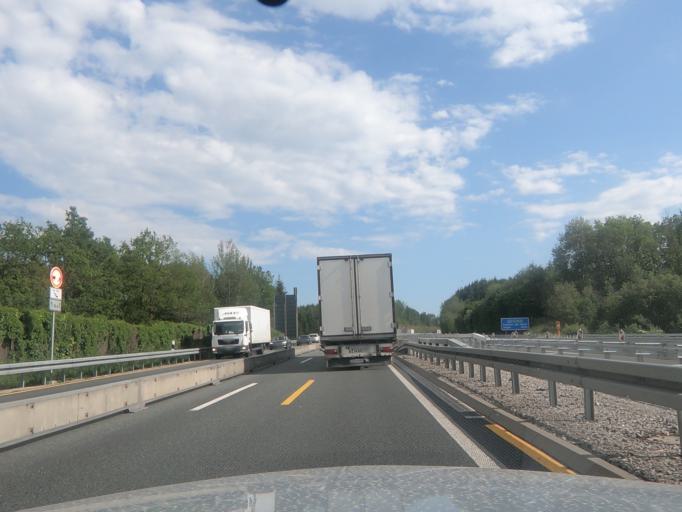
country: DE
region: North Rhine-Westphalia
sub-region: Regierungsbezirk Arnsberg
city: Wenden
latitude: 50.9787
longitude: 7.8416
